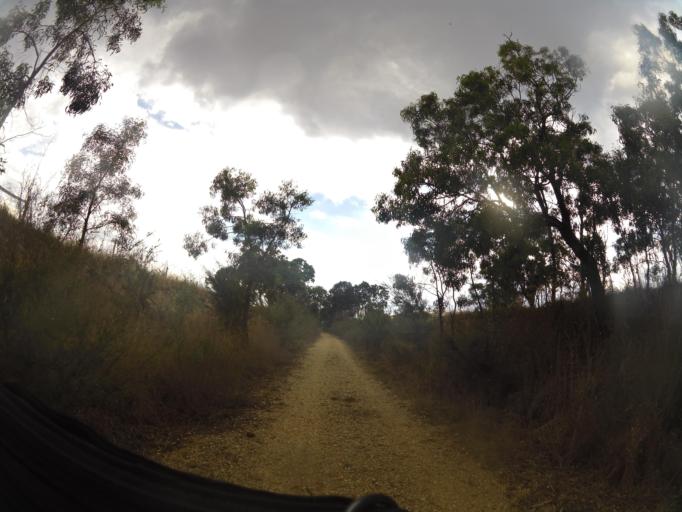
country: AU
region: Victoria
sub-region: Wellington
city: Heyfield
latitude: -38.0243
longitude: 146.6727
